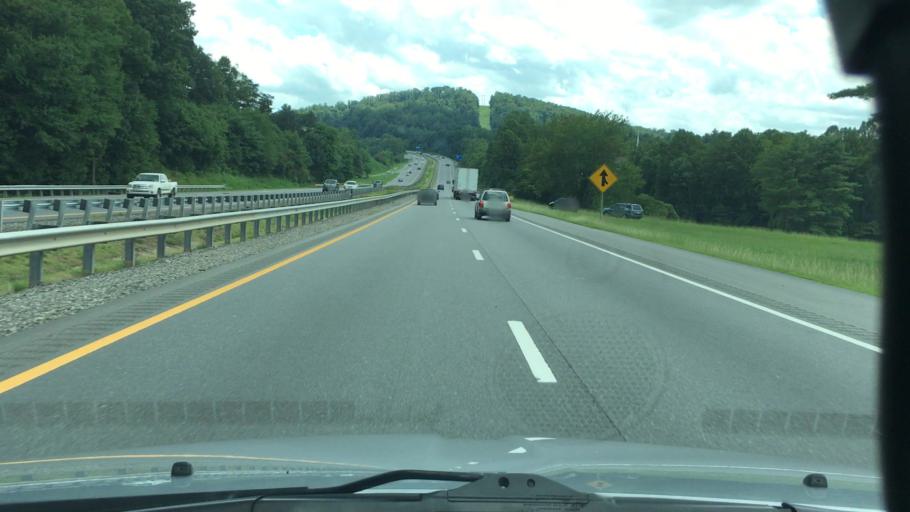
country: US
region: North Carolina
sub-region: Buncombe County
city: Weaverville
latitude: 35.6759
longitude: -82.5835
